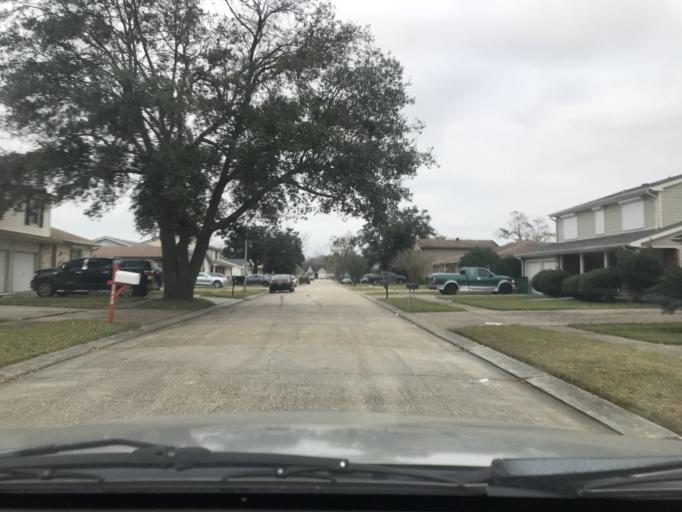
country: US
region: Louisiana
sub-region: Jefferson Parish
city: Woodmere
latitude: 29.8590
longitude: -90.0765
